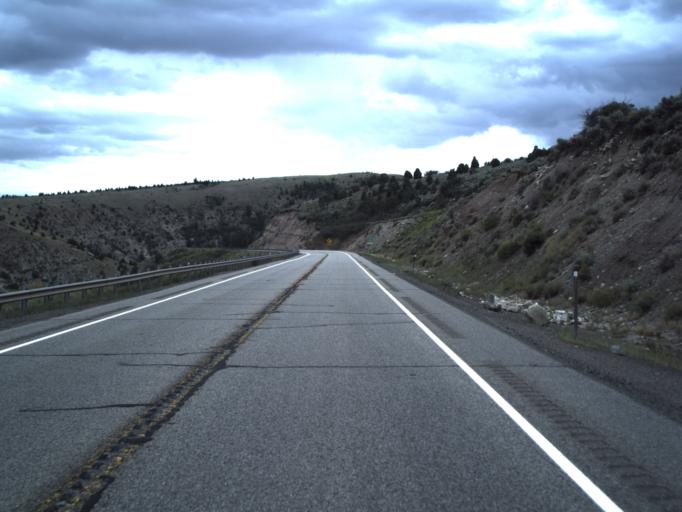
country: US
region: Utah
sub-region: Carbon County
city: Helper
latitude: 39.8203
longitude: -110.9432
